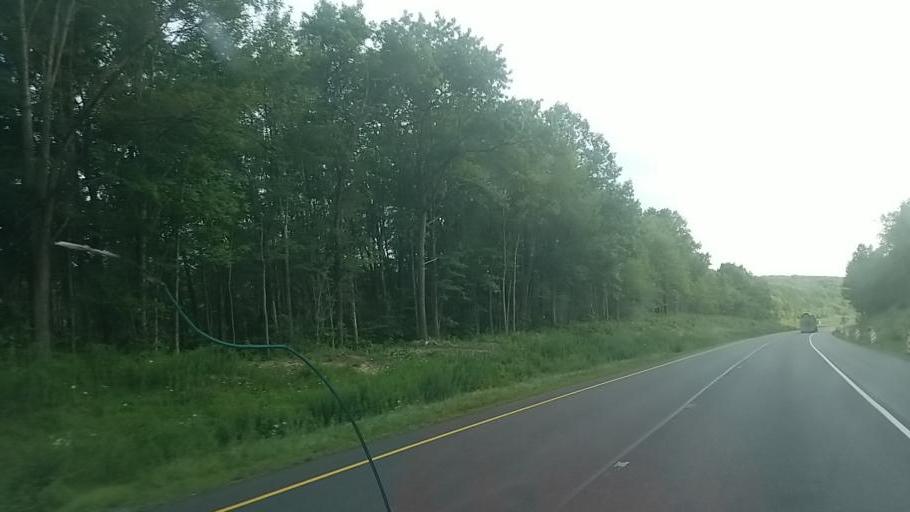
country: US
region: Pennsylvania
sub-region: Centre County
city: Milesburg
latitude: 41.0106
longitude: -77.9631
